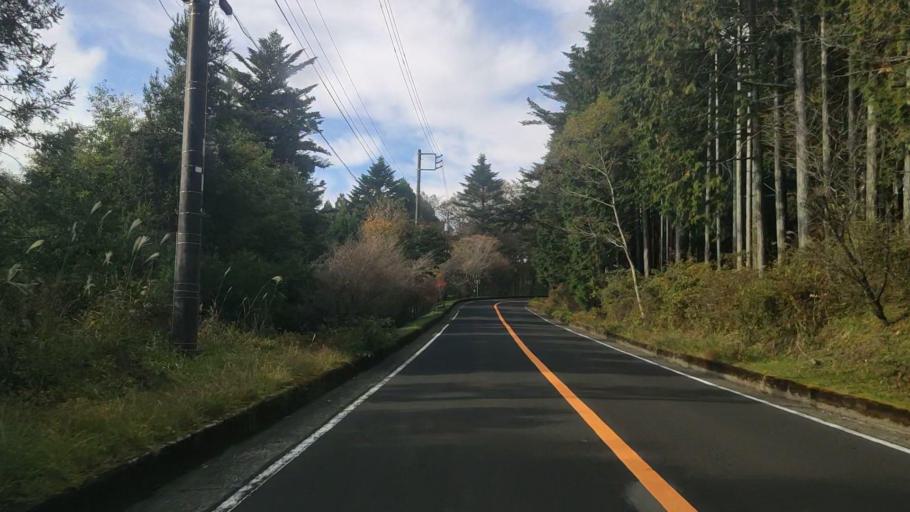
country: JP
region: Shizuoka
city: Fujinomiya
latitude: 35.3033
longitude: 138.6744
